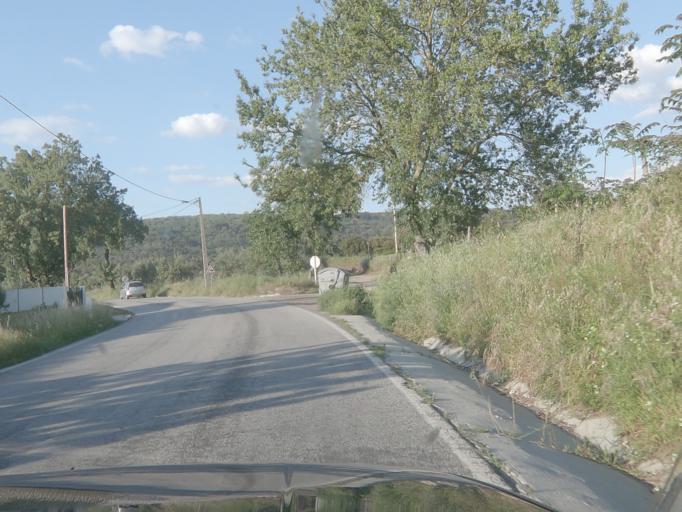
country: PT
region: Portalegre
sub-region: Portalegre
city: Portalegre
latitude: 39.3209
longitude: -7.4376
